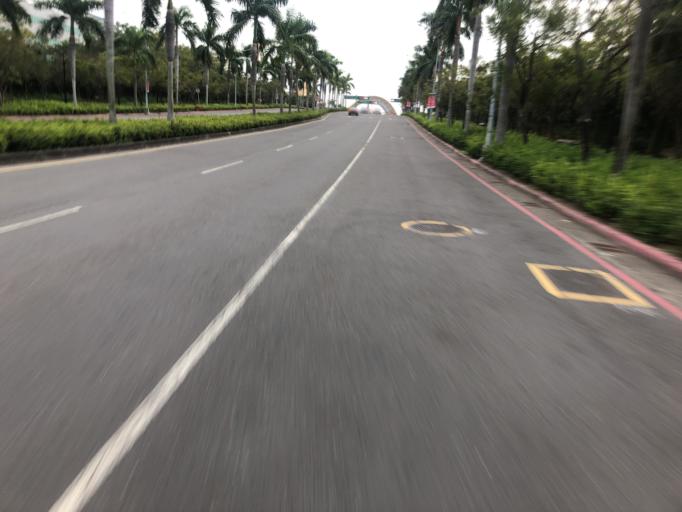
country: TW
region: Taiwan
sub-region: Tainan
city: Tainan
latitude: 23.0930
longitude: 120.2819
